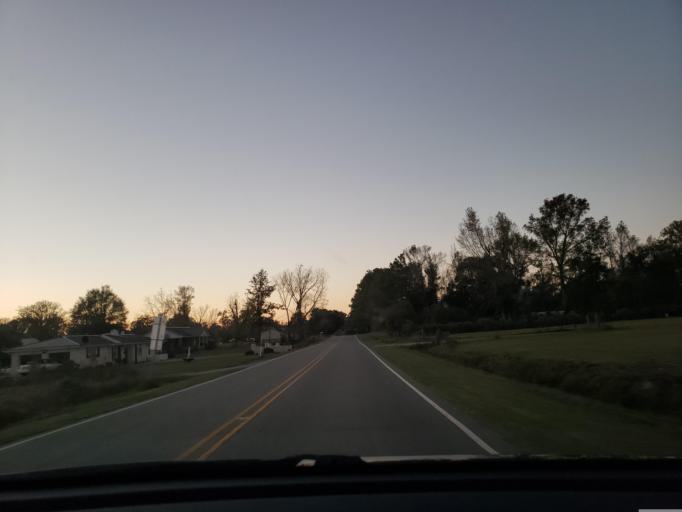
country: US
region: North Carolina
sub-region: Duplin County
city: Beulaville
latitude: 34.7998
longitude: -77.7789
